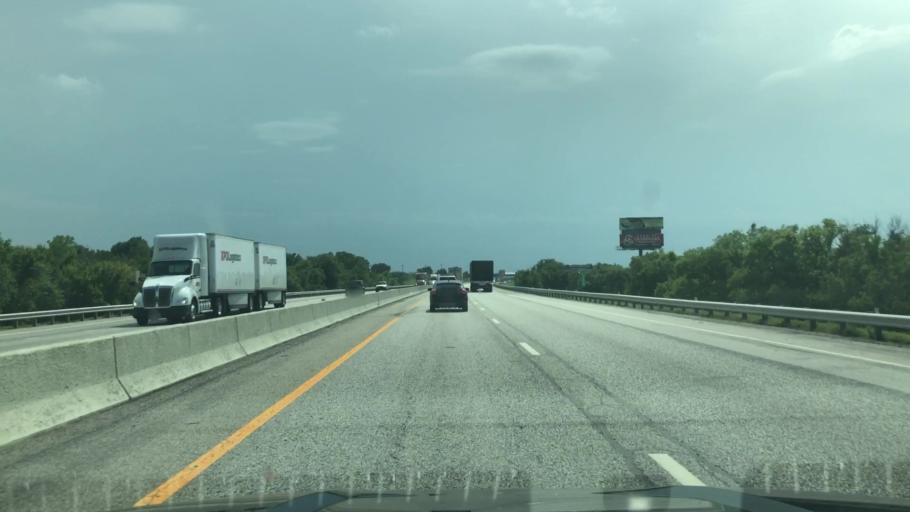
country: US
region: Oklahoma
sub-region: Craig County
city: Vinita
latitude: 36.6294
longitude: -95.1379
